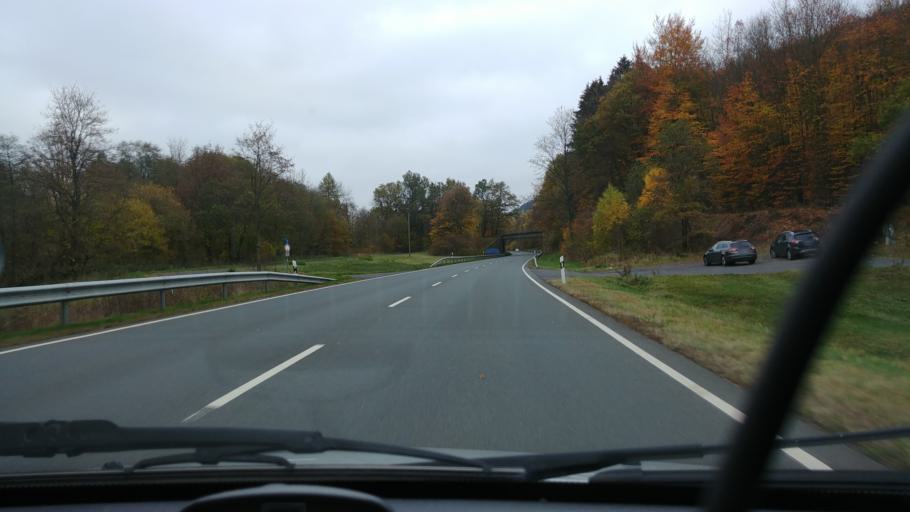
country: DE
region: Rheinland-Pfalz
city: Unnau
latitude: 50.6595
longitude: 7.8827
